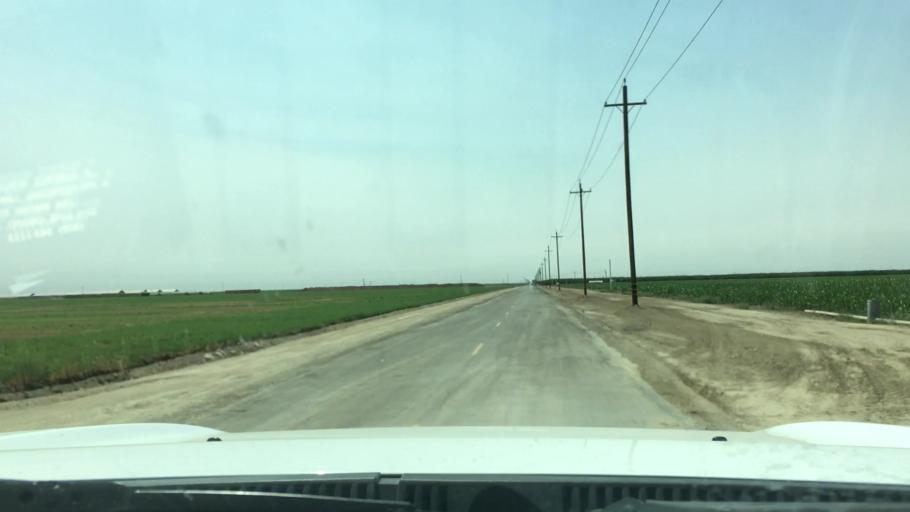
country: US
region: California
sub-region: Tulare County
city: Alpaugh
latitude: 35.7318
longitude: -119.4371
